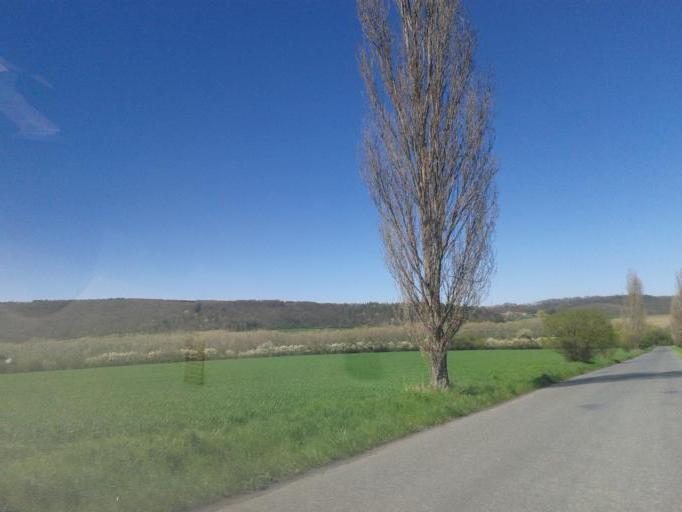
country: CZ
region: Central Bohemia
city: Revnice
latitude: 49.8793
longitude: 14.1469
